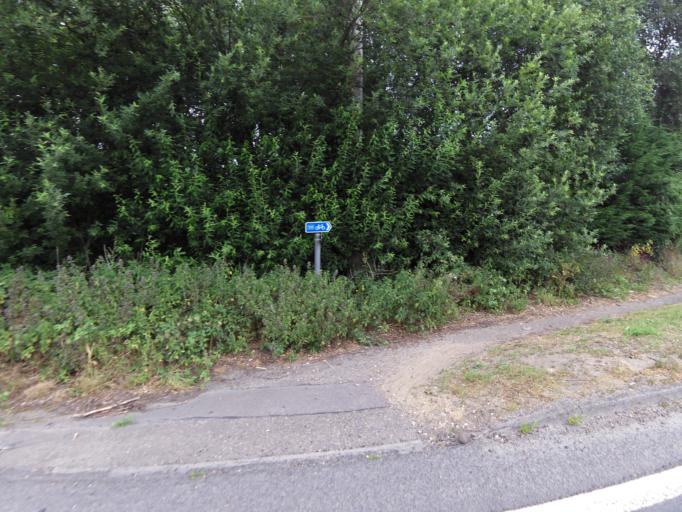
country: GB
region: England
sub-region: Norfolk
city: Harleston
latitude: 52.4232
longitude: 1.3542
